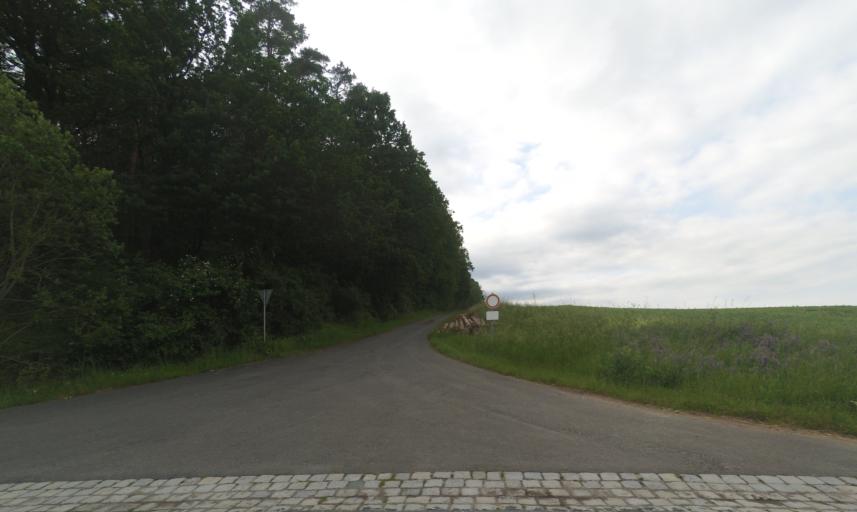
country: DE
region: Bavaria
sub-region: Upper Franconia
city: Schlusselfeld
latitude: 49.7825
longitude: 10.6527
